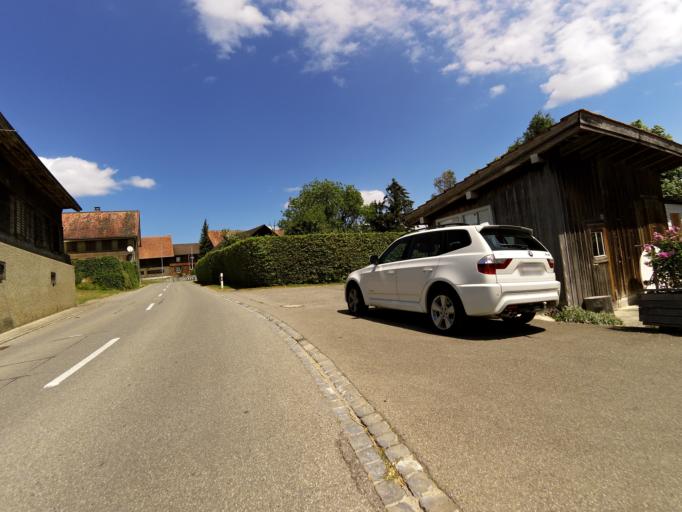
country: CH
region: Thurgau
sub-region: Weinfelden District
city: Maerstetten-Dorf
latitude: 47.6068
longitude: 9.0636
